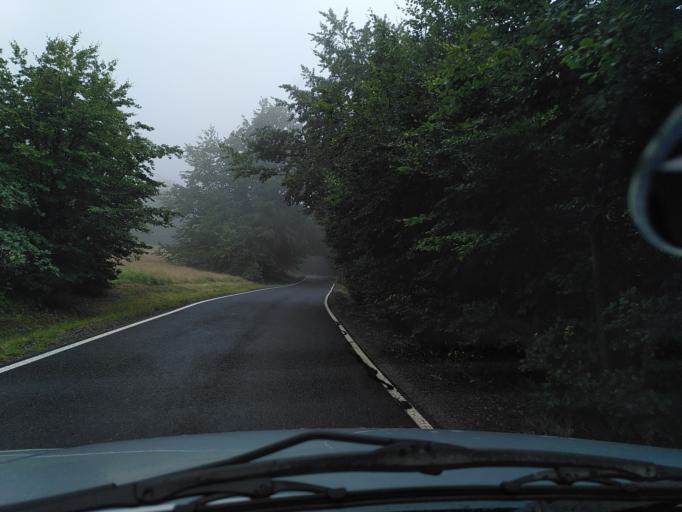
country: CZ
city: Kamenicky Senov
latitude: 50.7833
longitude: 14.5127
